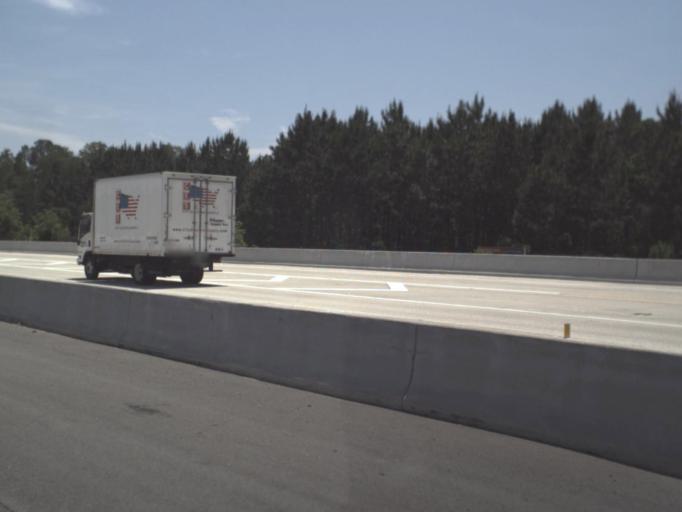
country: US
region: Florida
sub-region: Clay County
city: Bellair-Meadowbrook Terrace
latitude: 30.2023
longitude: -81.7533
